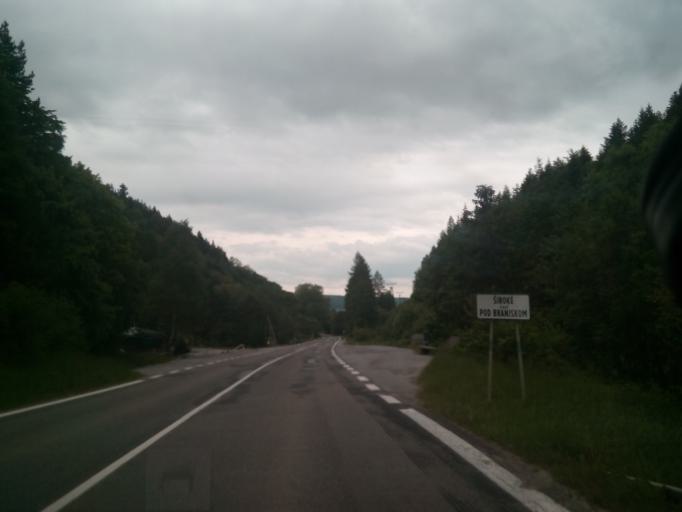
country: SK
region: Kosicky
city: Krompachy
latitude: 48.9964
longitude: 20.8957
